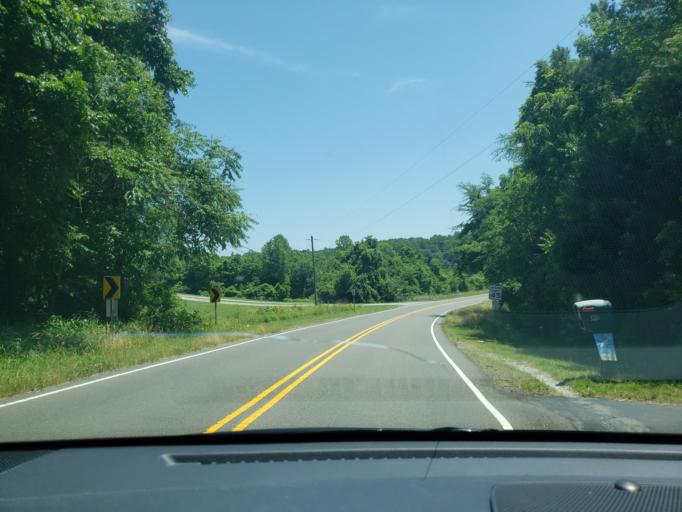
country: US
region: North Carolina
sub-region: Durham County
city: Gorman
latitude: 36.1277
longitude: -78.8780
